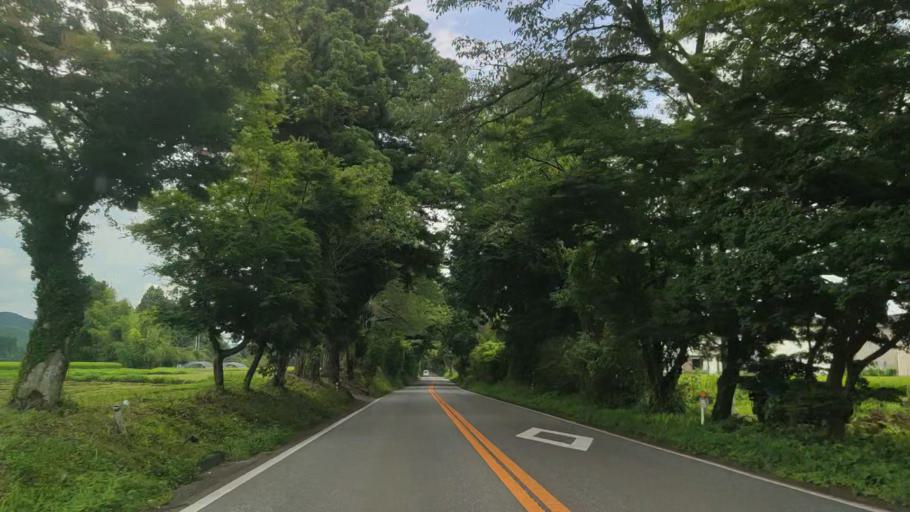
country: JP
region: Tochigi
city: Imaichi
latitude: 36.6886
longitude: 139.7702
